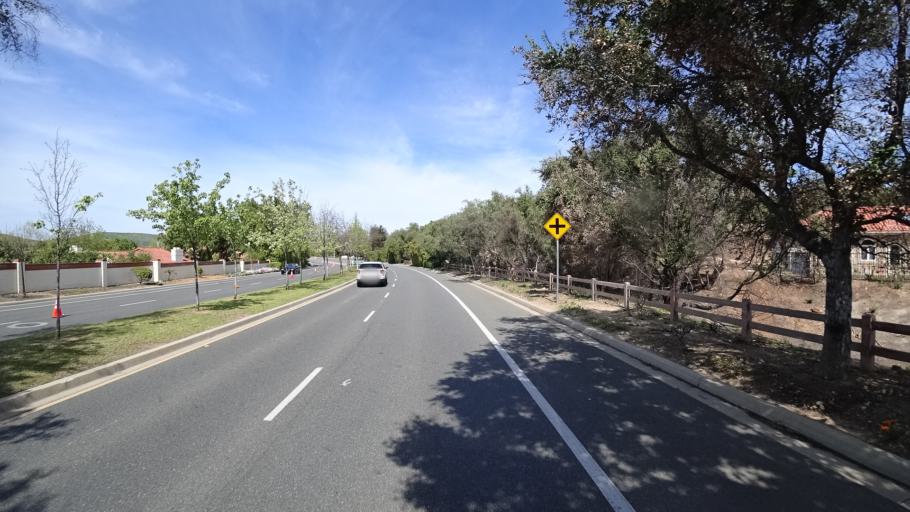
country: US
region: California
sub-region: Ventura County
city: Thousand Oaks
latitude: 34.1988
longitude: -118.8118
